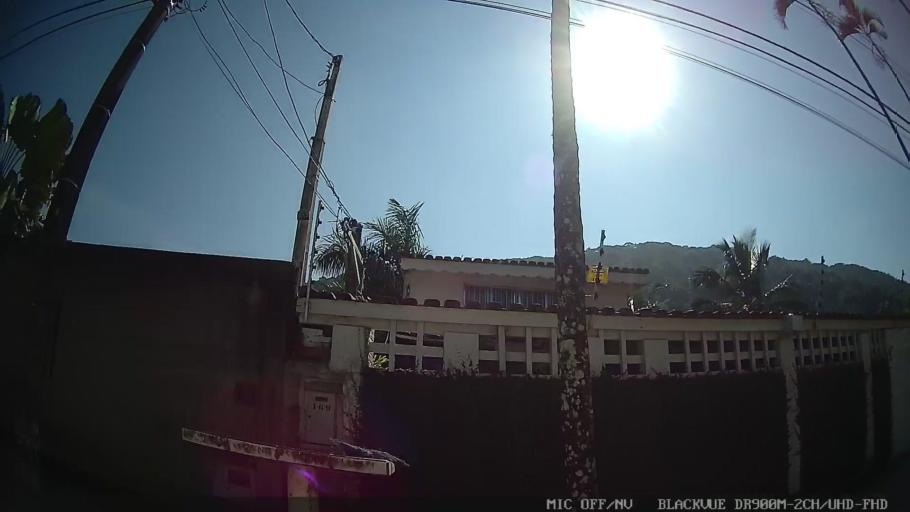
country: BR
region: Sao Paulo
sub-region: Guaruja
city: Guaruja
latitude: -24.0142
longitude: -46.2885
